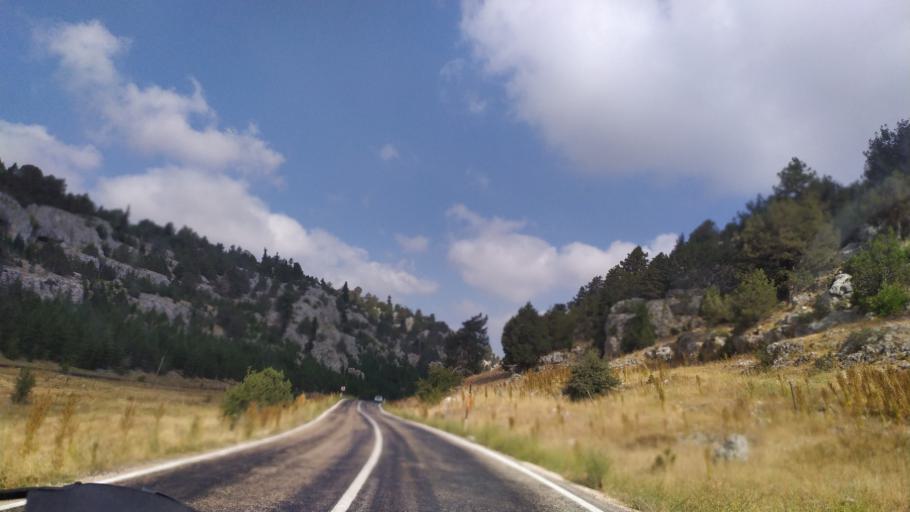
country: TR
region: Mersin
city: Kirobasi
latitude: 36.6153
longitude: 33.8772
